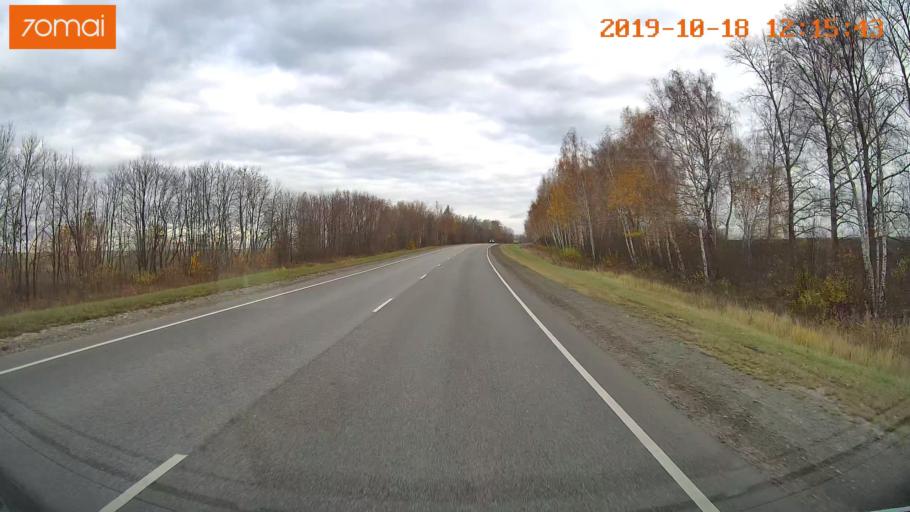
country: RU
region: Rjazan
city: Zakharovo
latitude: 54.4473
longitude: 39.4049
